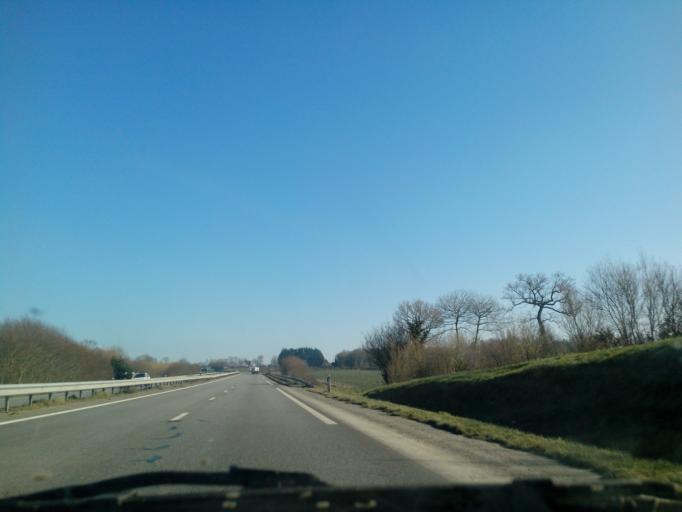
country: FR
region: Brittany
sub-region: Departement des Cotes-d'Armor
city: Loudeac
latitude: 48.1794
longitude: -2.7215
